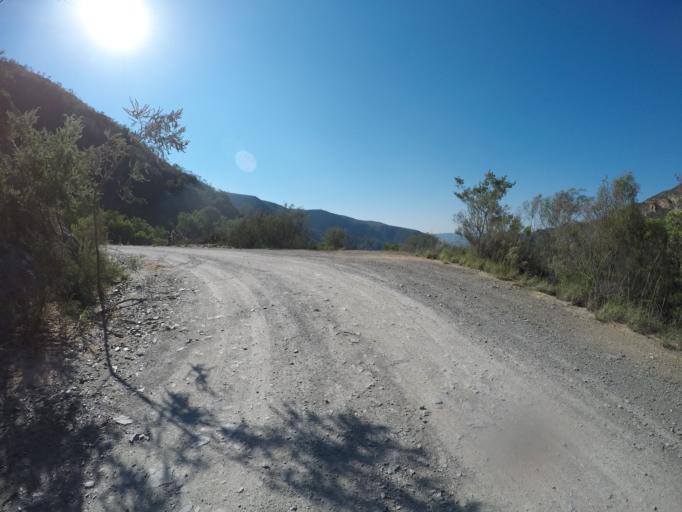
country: ZA
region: Eastern Cape
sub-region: Cacadu District Municipality
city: Kareedouw
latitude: -33.6558
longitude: 24.5054
